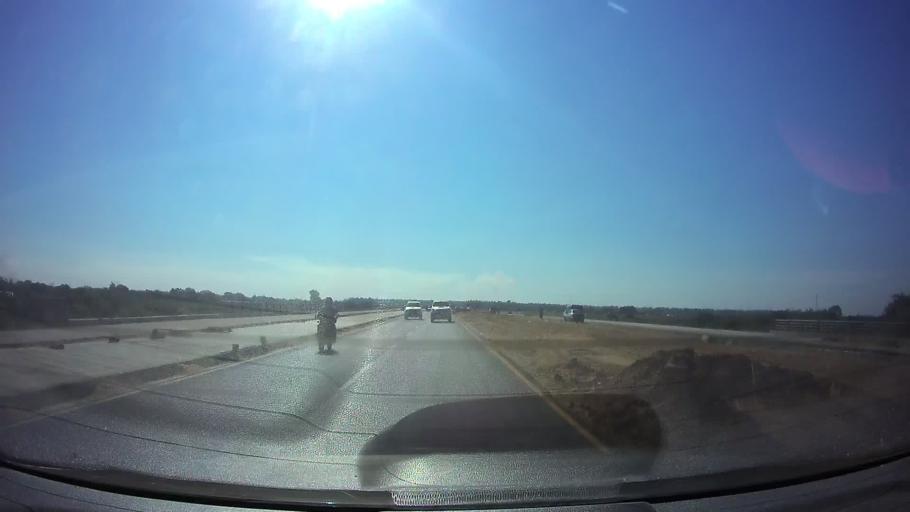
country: PY
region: Asuncion
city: Asuncion
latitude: -25.2593
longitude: -57.6077
